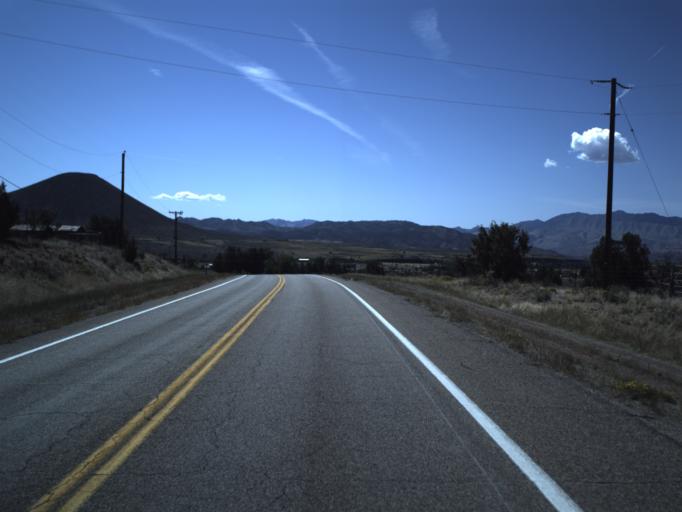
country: US
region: Utah
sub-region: Washington County
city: Ivins
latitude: 37.3454
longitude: -113.6924
